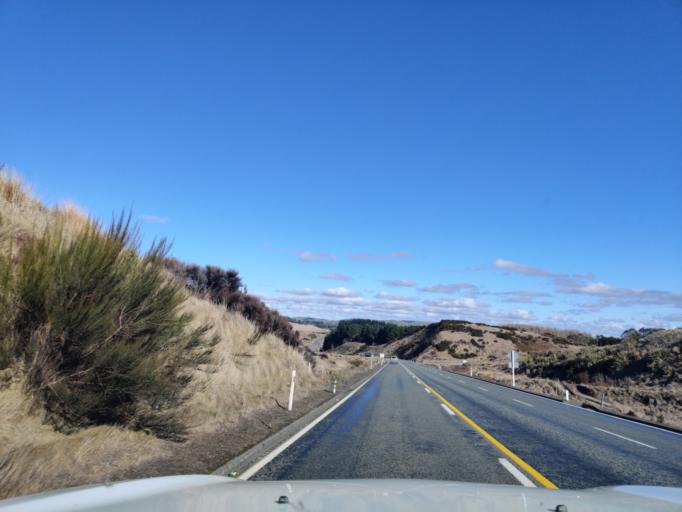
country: NZ
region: Manawatu-Wanganui
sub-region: Ruapehu District
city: Waiouru
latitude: -39.4360
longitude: 175.6834
